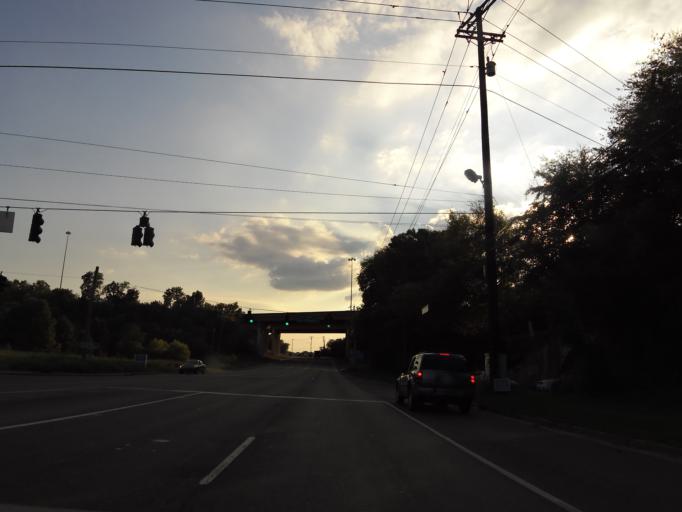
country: US
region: Tennessee
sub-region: Knox County
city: Knoxville
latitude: 36.0182
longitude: -83.8590
